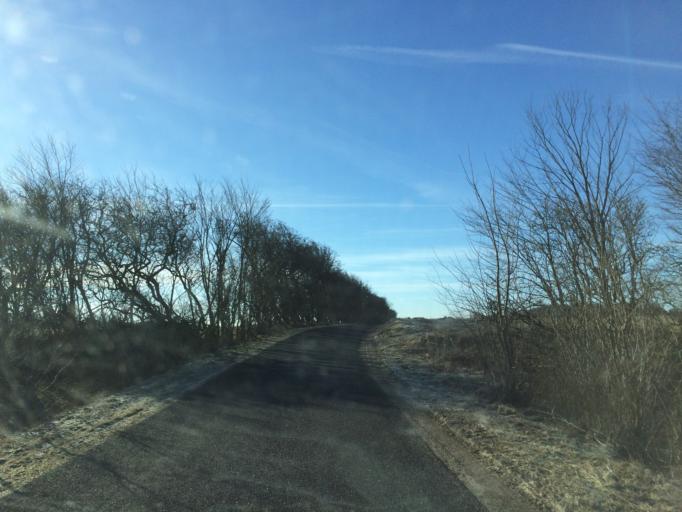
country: DK
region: North Denmark
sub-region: Mariagerfjord Kommune
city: Hobro
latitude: 56.6225
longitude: 9.6439
